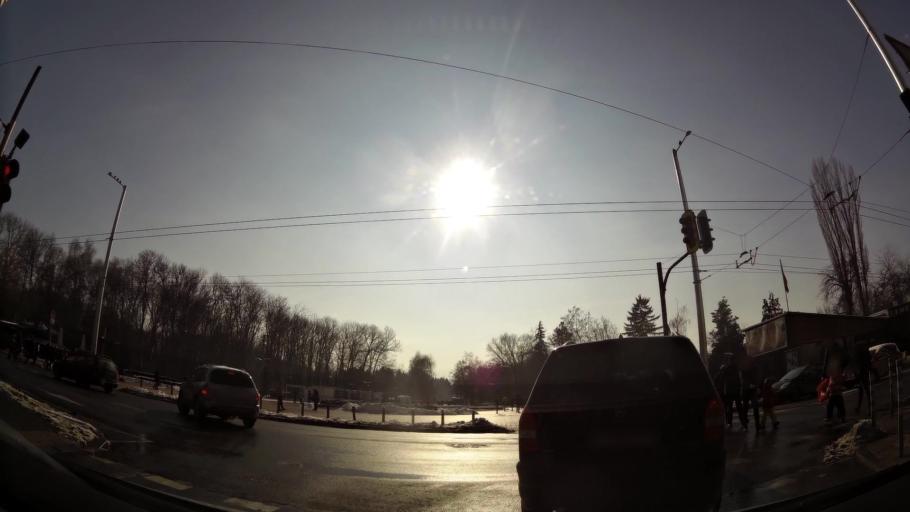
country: BG
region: Sofia-Capital
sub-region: Stolichna Obshtina
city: Sofia
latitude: 42.6749
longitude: 23.3089
